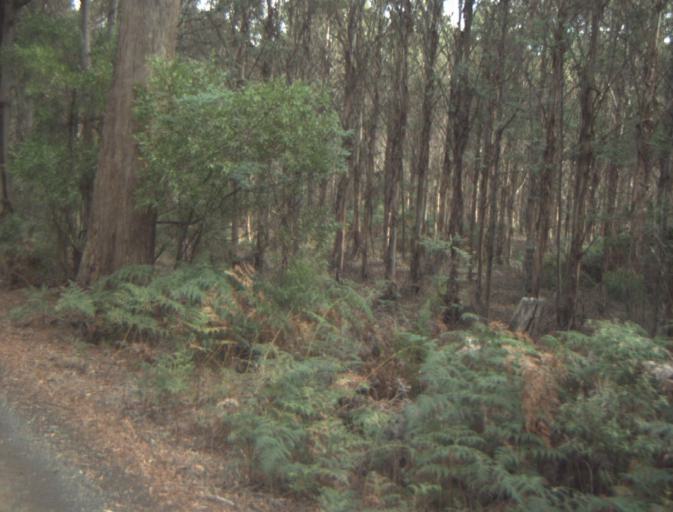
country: AU
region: Tasmania
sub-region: Launceston
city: Mayfield
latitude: -41.2142
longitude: 147.1775
